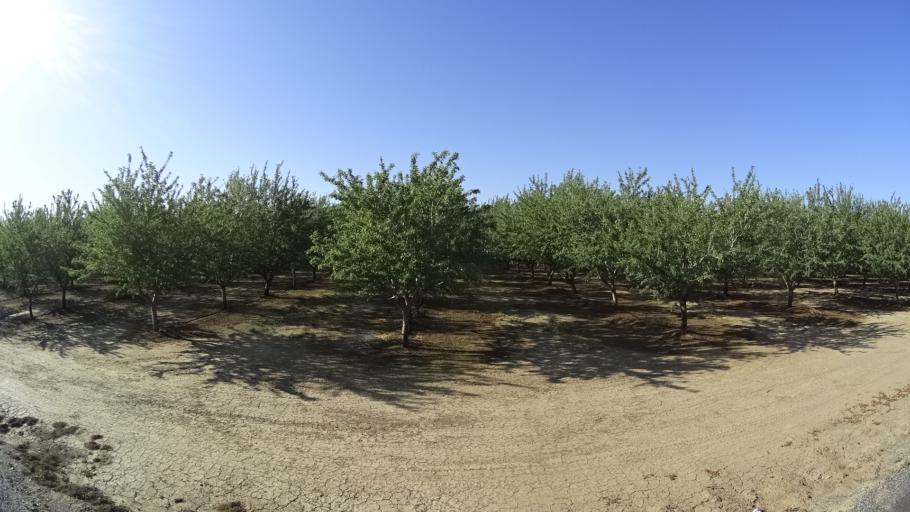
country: US
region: California
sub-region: Glenn County
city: Orland
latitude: 39.6960
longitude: -122.1106
